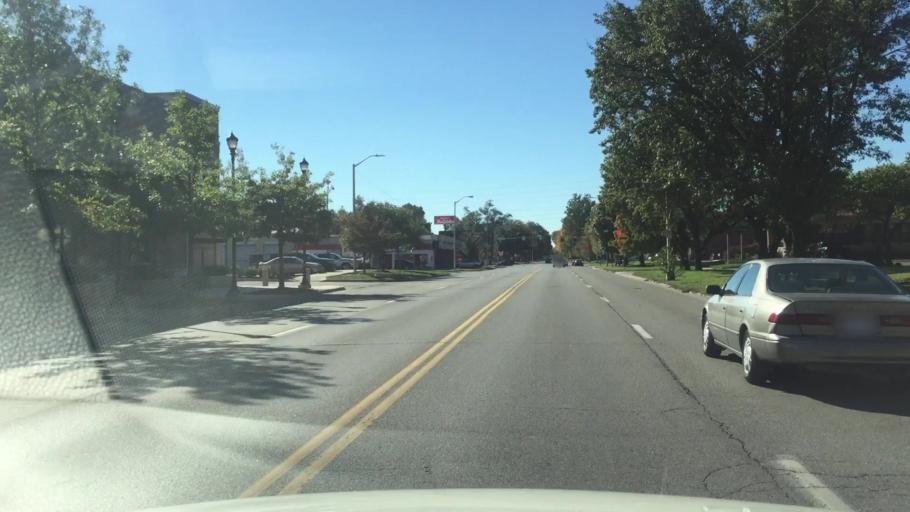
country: US
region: Kansas
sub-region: Douglas County
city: Lawrence
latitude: 38.9520
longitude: -95.2359
